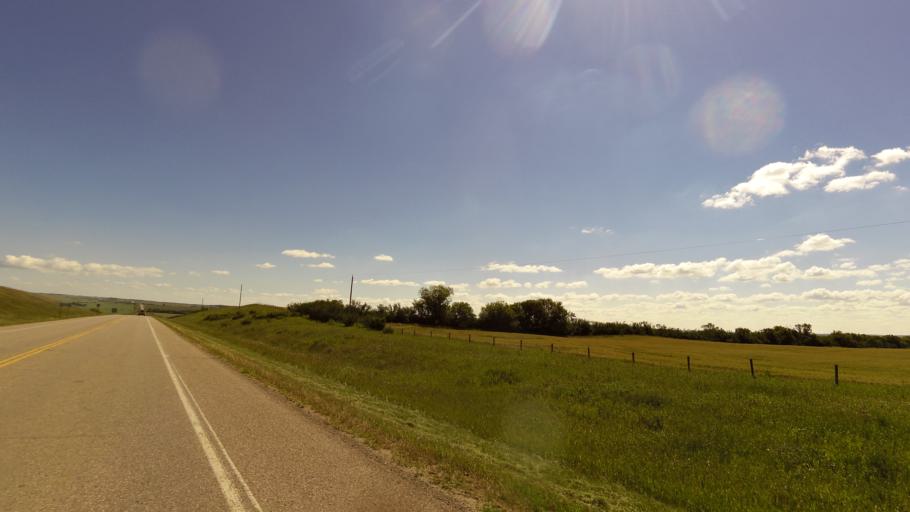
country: CA
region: Saskatchewan
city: Lloydminster
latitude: 52.8421
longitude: -110.0506
